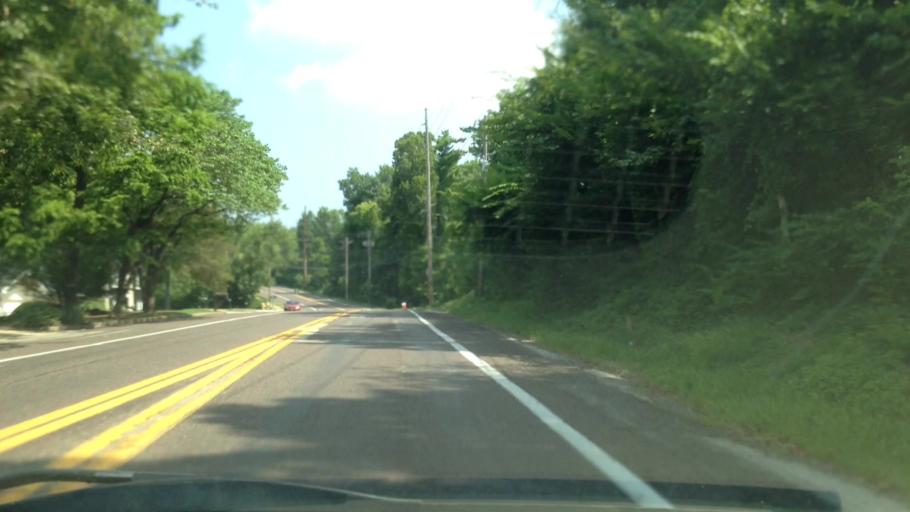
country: US
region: Missouri
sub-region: Saint Louis County
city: Des Peres
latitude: 38.5885
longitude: -90.4450
